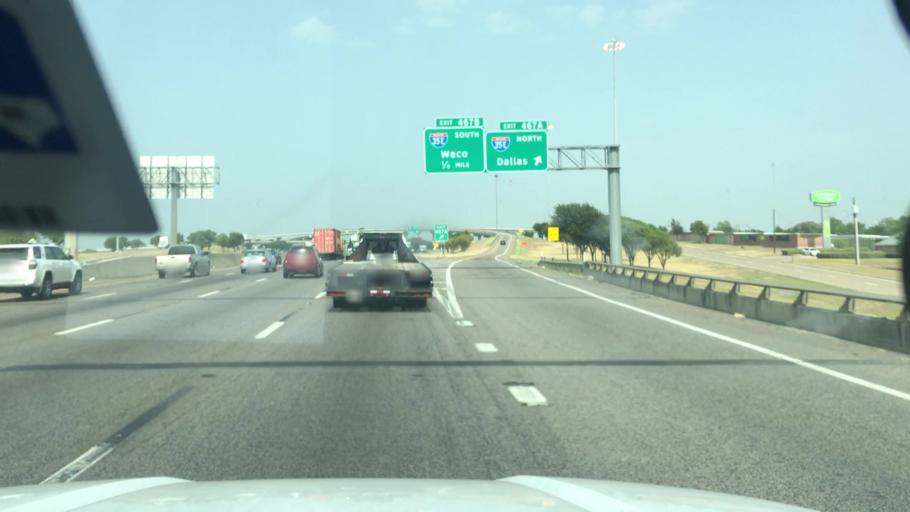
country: US
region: Texas
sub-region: Dallas County
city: DeSoto
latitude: 32.6420
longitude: -96.8295
